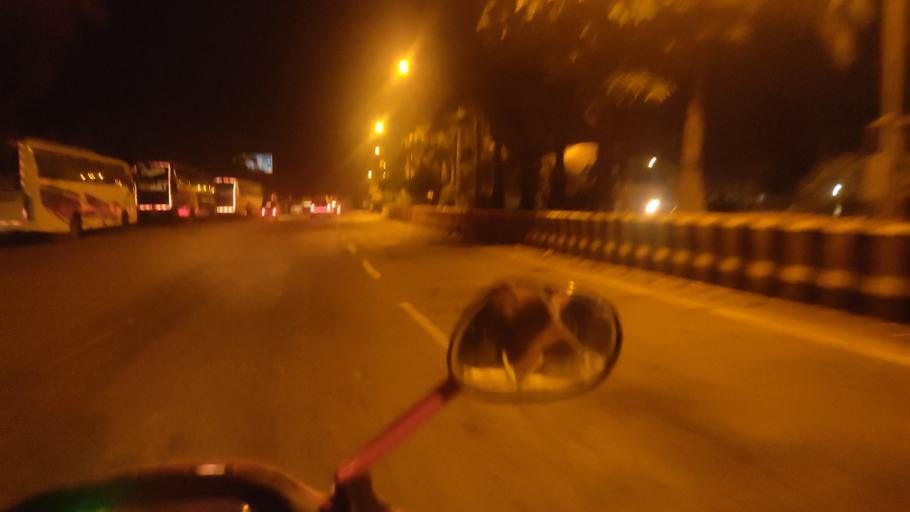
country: IN
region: Maharashtra
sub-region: Thane
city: Bhayandar
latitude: 19.2976
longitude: 72.8410
